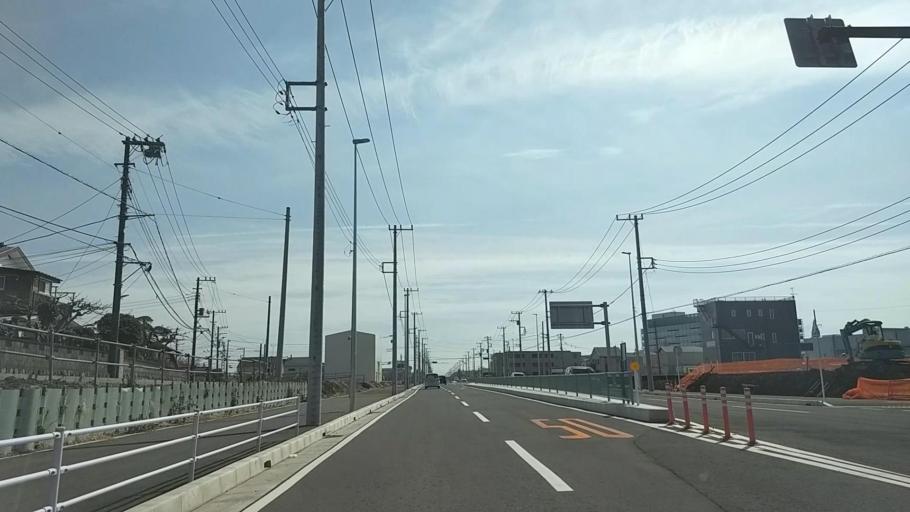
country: JP
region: Kanagawa
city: Fujisawa
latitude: 35.4068
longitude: 139.4538
